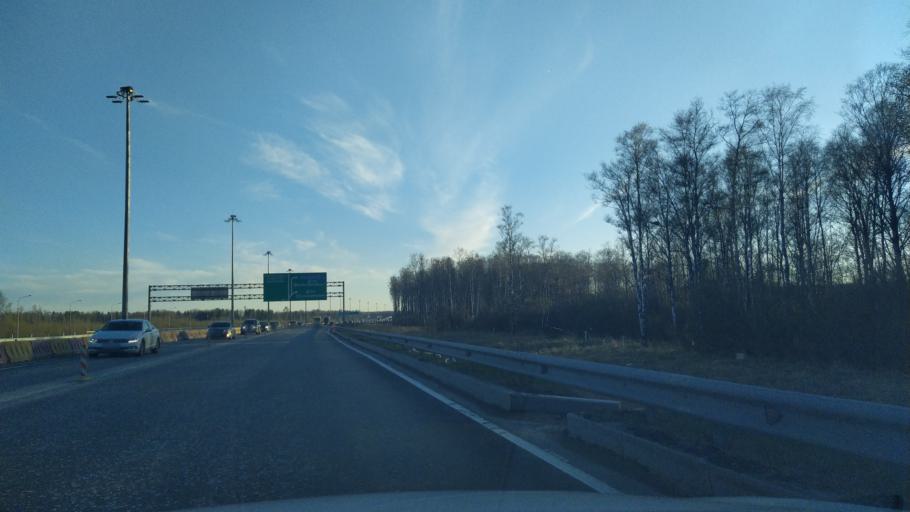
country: RU
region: St.-Petersburg
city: Levashovo
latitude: 60.0671
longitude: 30.1693
